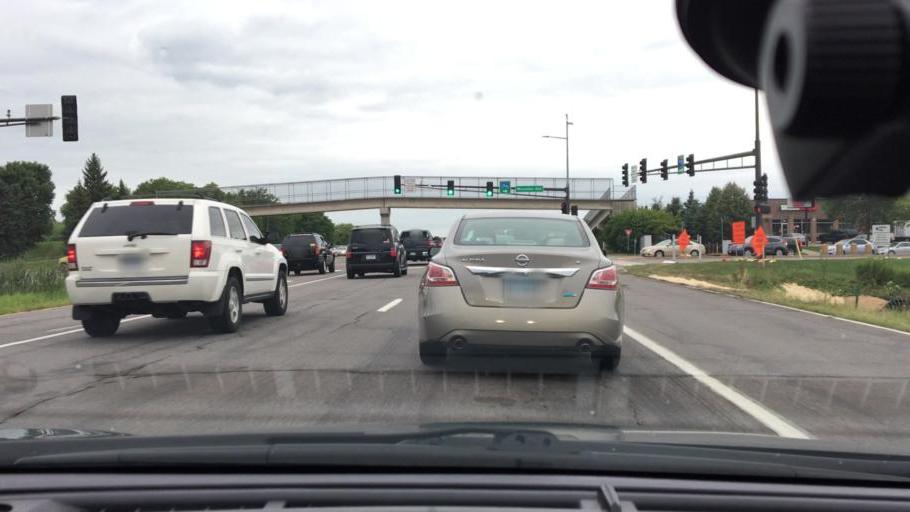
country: US
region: Minnesota
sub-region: Hennepin County
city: Golden Valley
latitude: 44.9837
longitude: -93.3797
